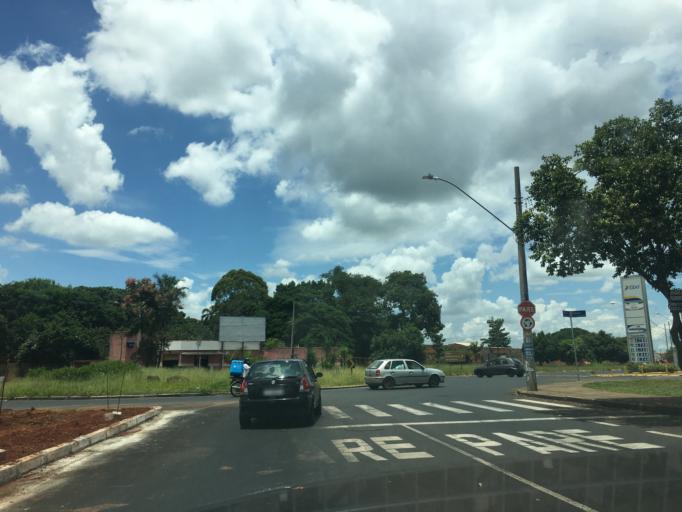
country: BR
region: Minas Gerais
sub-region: Uberlandia
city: Uberlandia
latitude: -18.9485
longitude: -48.3136
